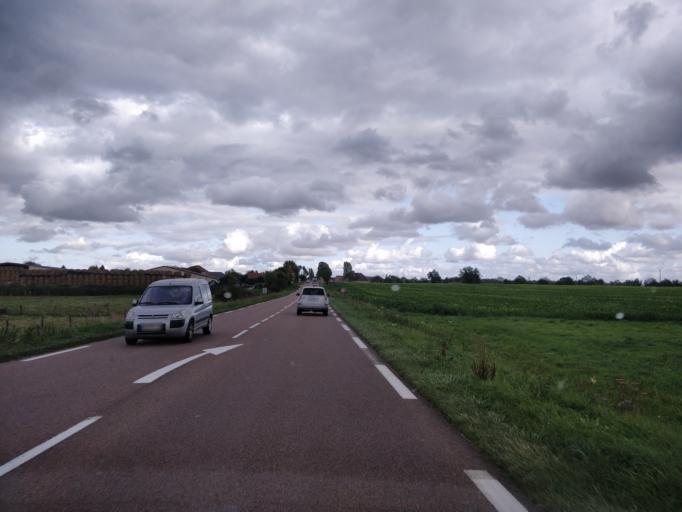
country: FR
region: Champagne-Ardenne
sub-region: Departement de l'Aube
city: Lusigny-sur-Barse
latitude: 48.2411
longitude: 4.2923
